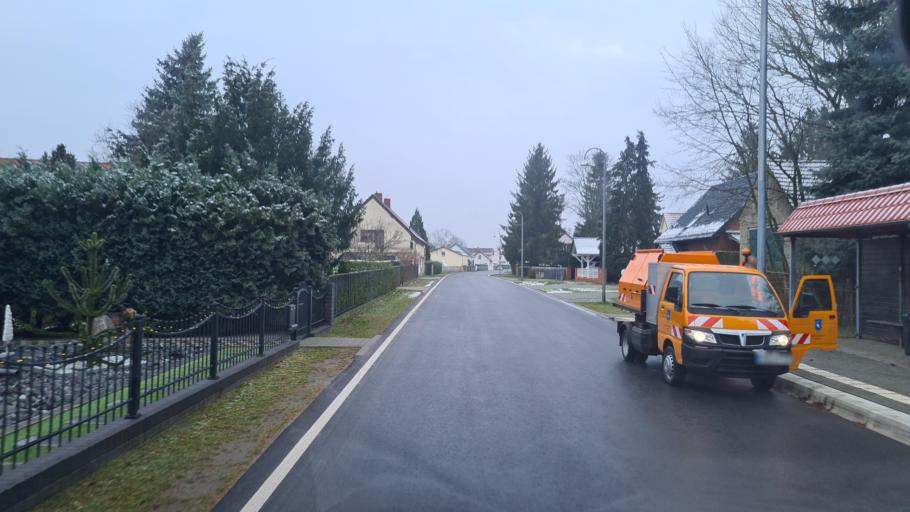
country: DE
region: Brandenburg
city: Storkow
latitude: 52.2852
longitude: 13.8803
